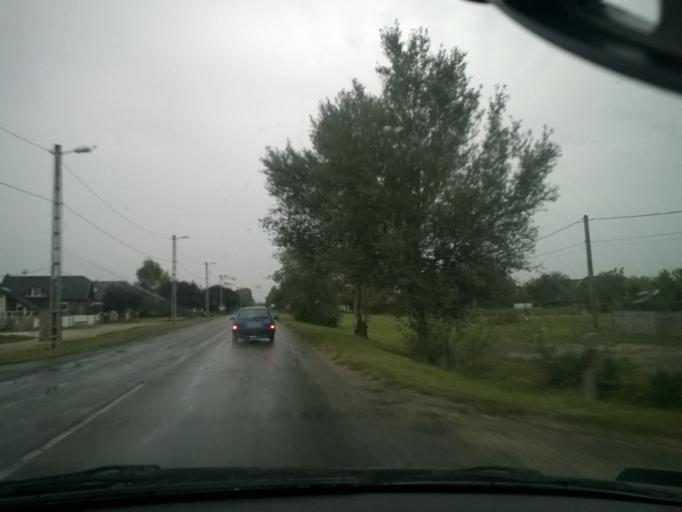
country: HU
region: Pest
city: Kiskunlachaza
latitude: 47.1659
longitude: 19.0000
